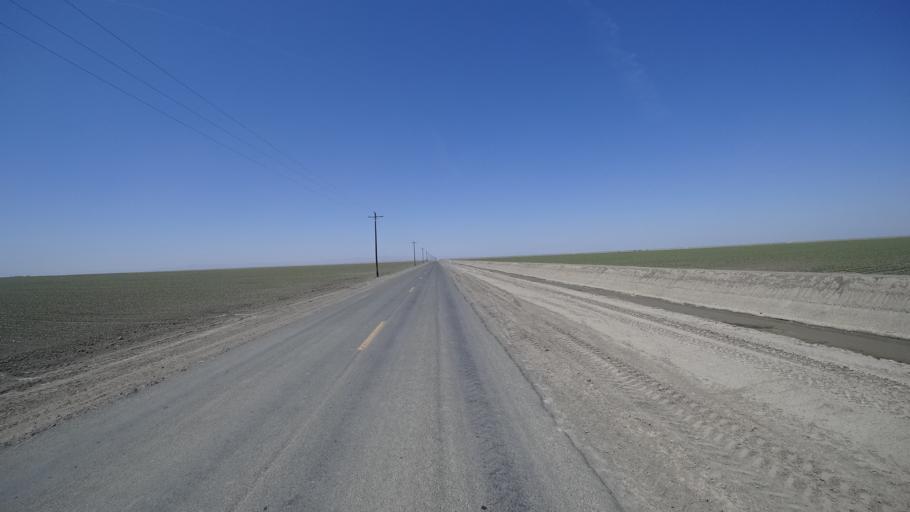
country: US
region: California
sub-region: Kings County
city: Corcoran
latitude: 36.0214
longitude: -119.6502
